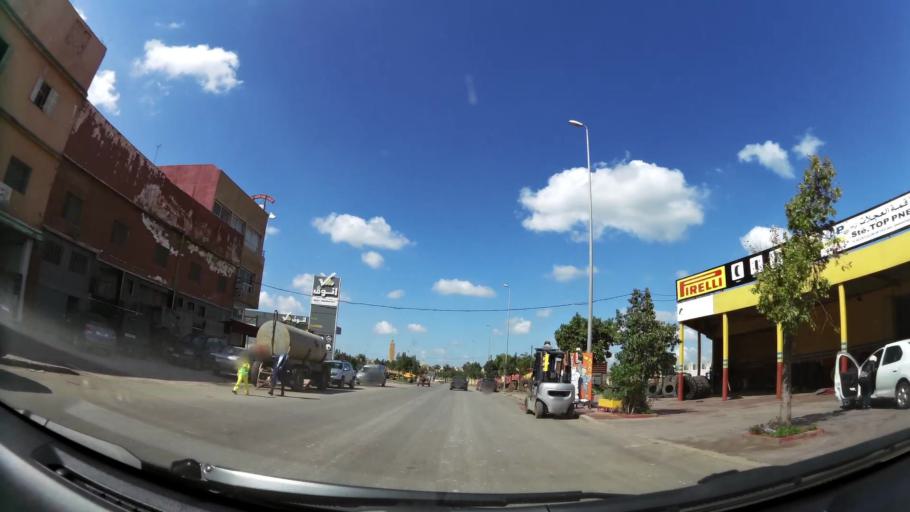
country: MA
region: Grand Casablanca
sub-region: Mediouna
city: Mediouna
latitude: 33.4494
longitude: -7.5179
